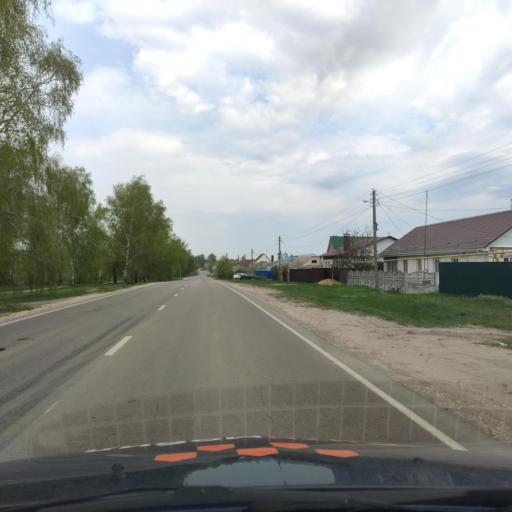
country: RU
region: Voronezj
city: Podgornoye
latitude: 51.8810
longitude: 39.1729
